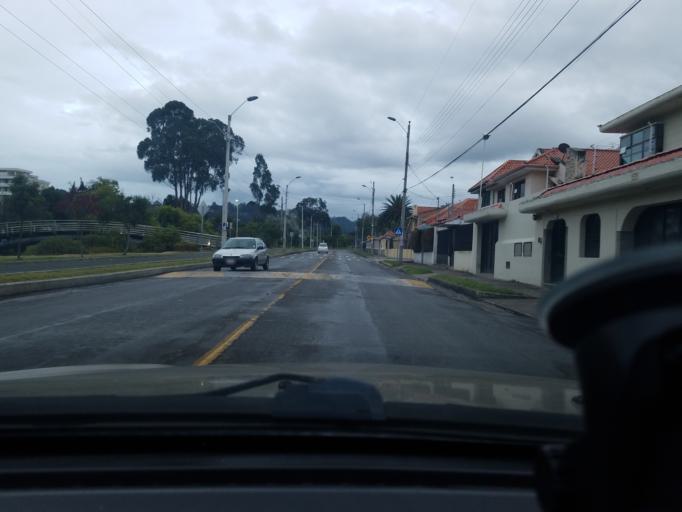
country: EC
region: Azuay
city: Cuenca
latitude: -2.9087
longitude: -78.9913
